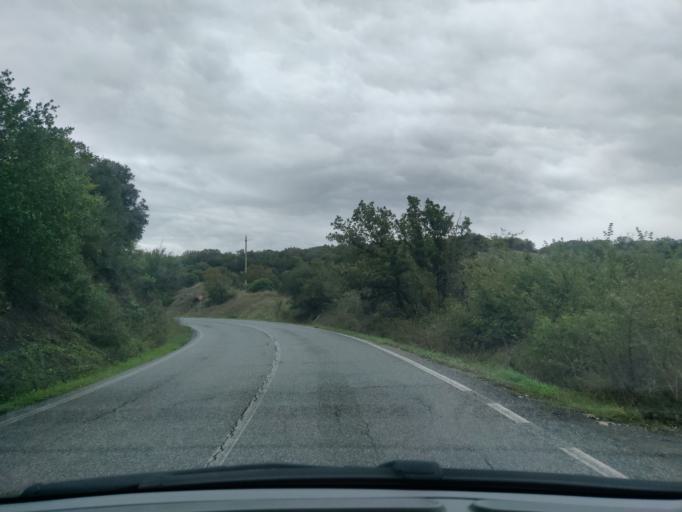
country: IT
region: Latium
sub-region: Citta metropolitana di Roma Capitale
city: Allumiere
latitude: 42.1368
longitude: 11.8715
